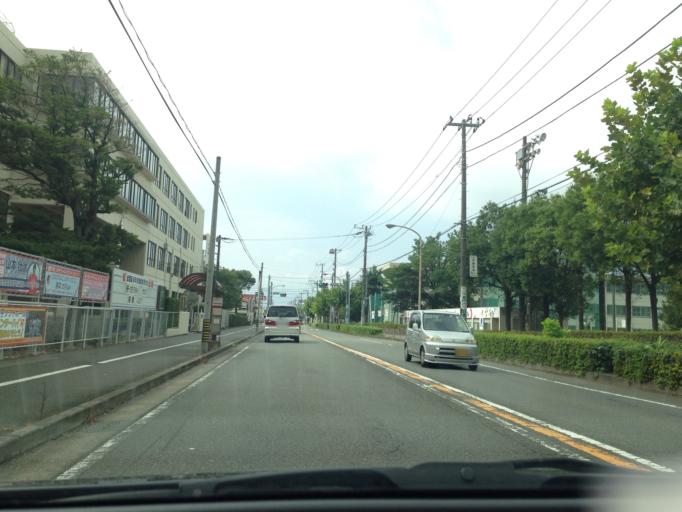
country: JP
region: Shizuoka
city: Numazu
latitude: 35.1171
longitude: 138.8672
